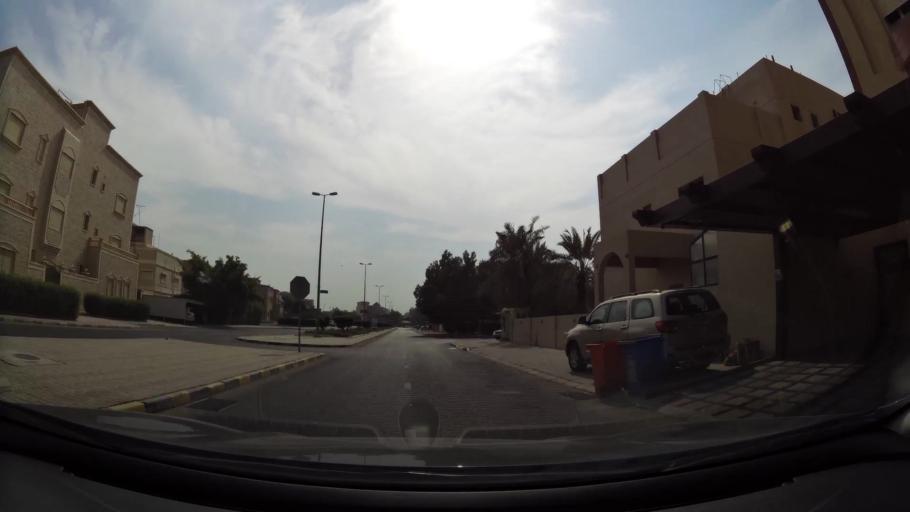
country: KW
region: Al Asimah
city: Ash Shamiyah
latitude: 29.3486
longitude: 47.9628
